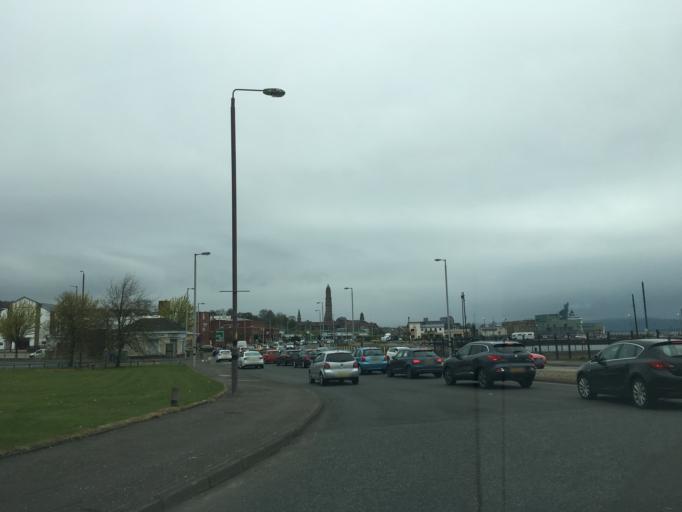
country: GB
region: Scotland
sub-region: Inverclyde
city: Greenock
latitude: 55.9436
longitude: -4.7442
